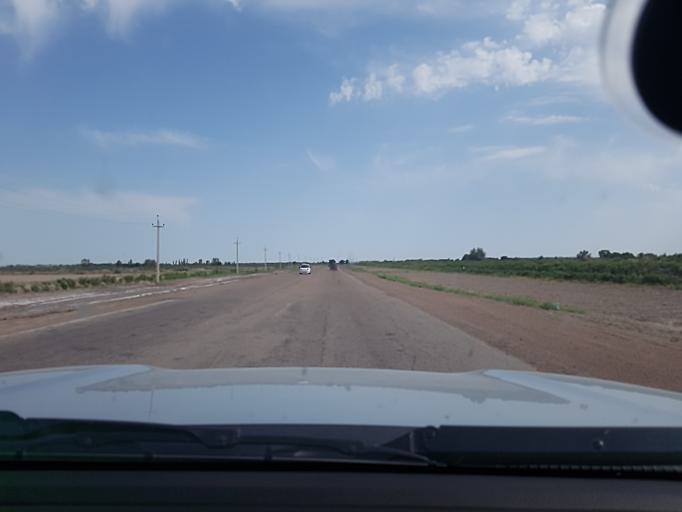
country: TM
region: Dasoguz
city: Boldumsaz
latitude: 42.0498
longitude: 59.7867
